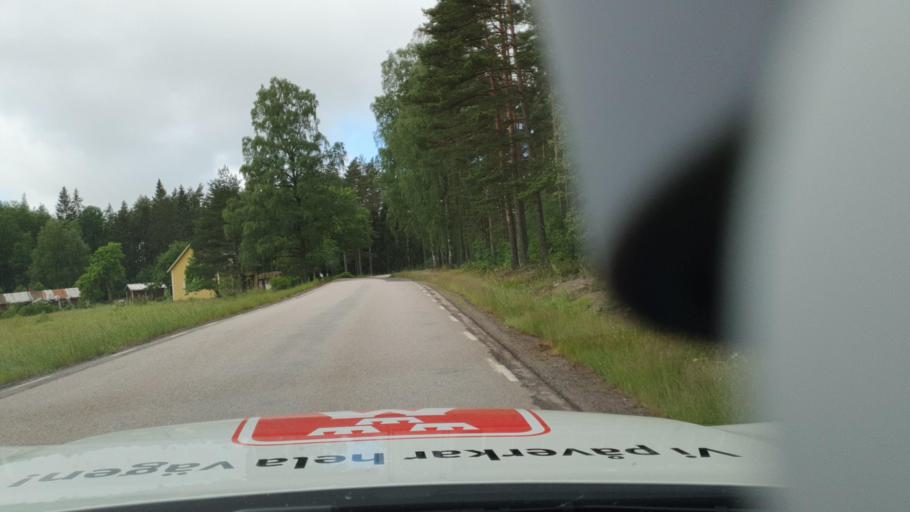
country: SE
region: Vaermland
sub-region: Kristinehamns Kommun
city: Bjorneborg
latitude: 59.1030
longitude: 14.3236
